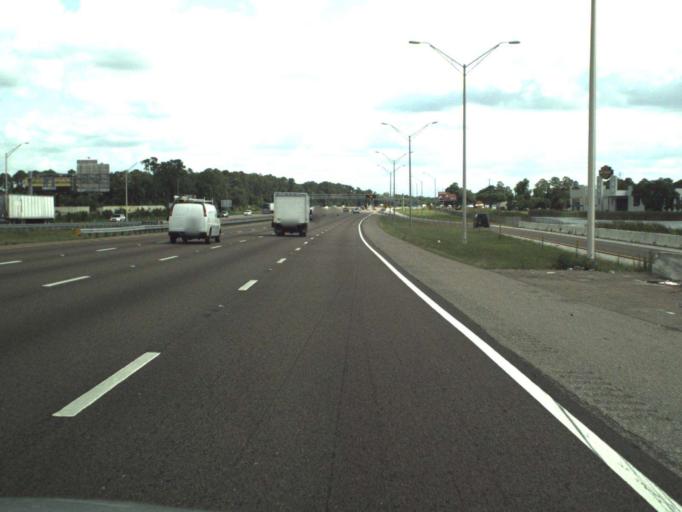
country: US
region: Florida
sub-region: Seminole County
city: Lake Mary
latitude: 28.8147
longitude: -81.3360
